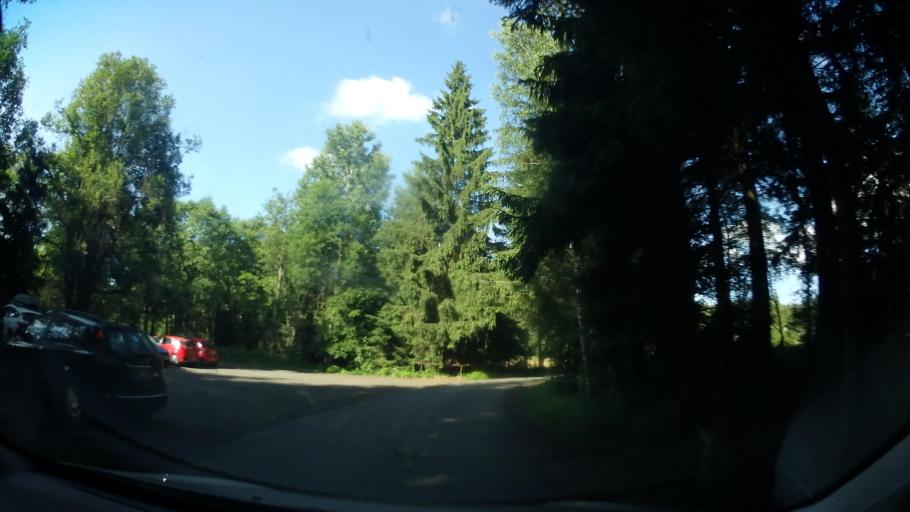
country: CZ
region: Vysocina
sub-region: Okres Zd'ar nad Sazavou
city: Svratka
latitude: 49.7292
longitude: 16.0459
